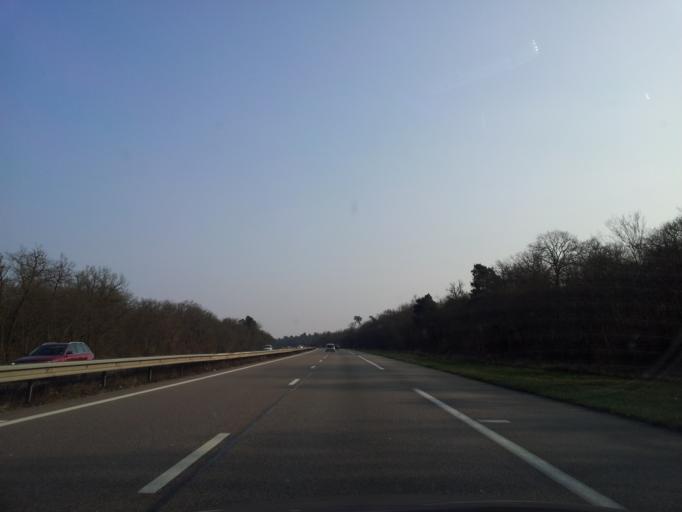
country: FR
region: Alsace
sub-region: Departement du Haut-Rhin
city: Sierentz
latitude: 47.6964
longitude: 7.4436
